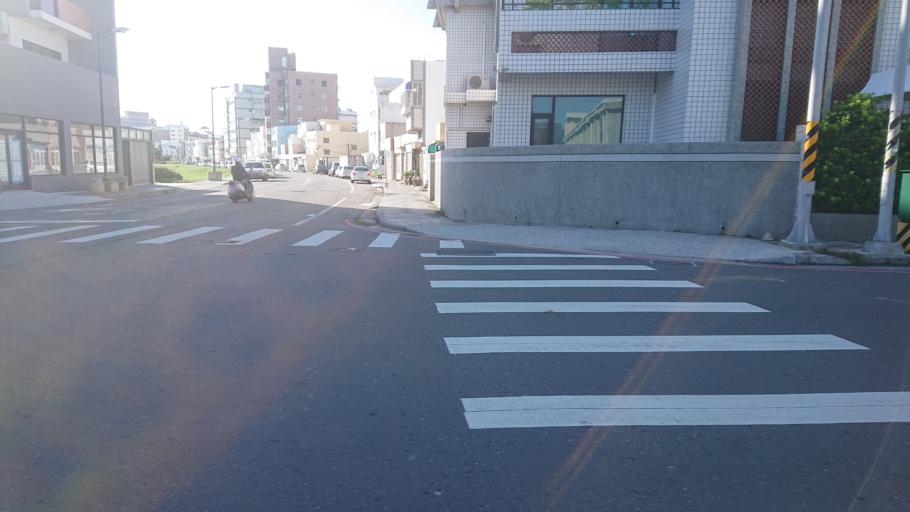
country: TW
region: Taiwan
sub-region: Penghu
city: Ma-kung
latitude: 23.5768
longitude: 119.5760
